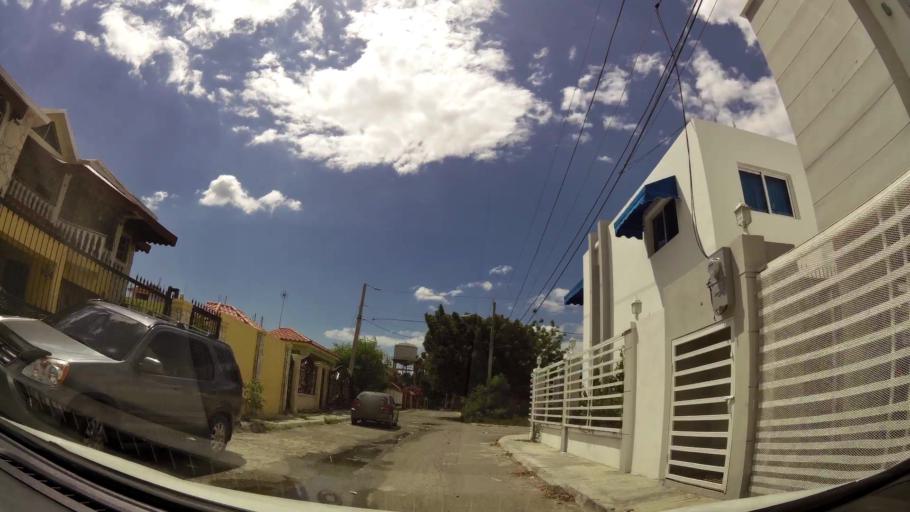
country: DO
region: San Cristobal
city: San Cristobal
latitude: 18.4167
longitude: -70.1025
